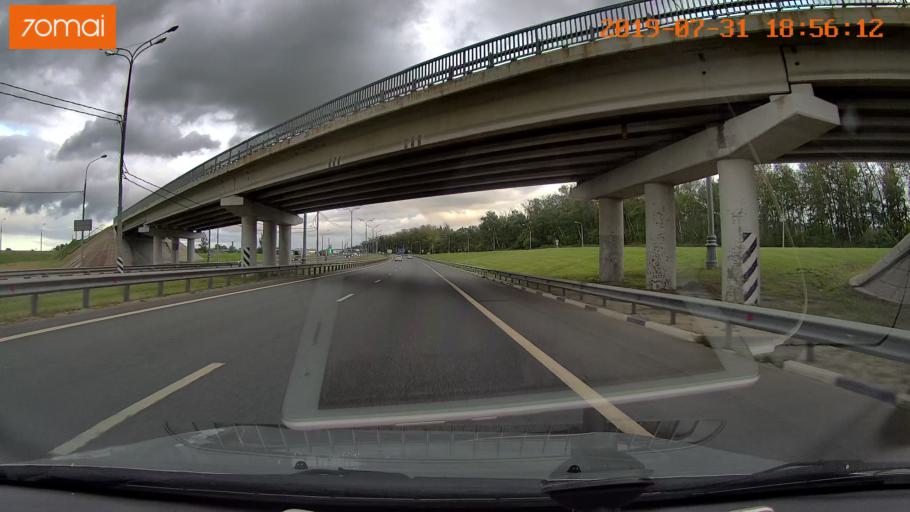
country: RU
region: Moskovskaya
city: Raduzhnyy
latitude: 55.1658
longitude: 38.6744
